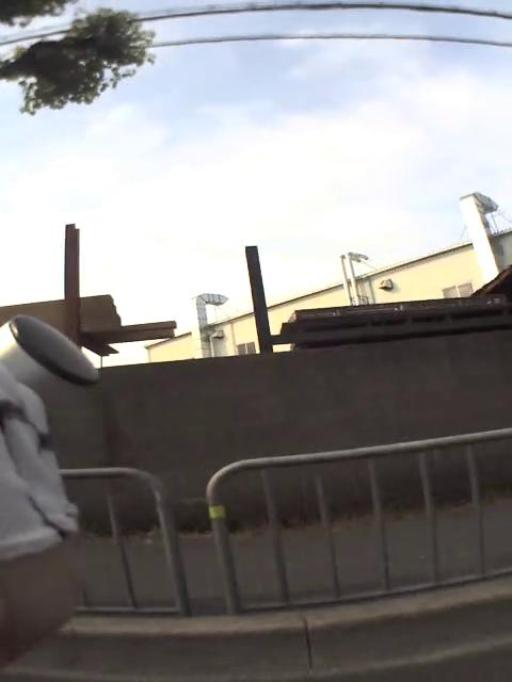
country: JP
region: Osaka
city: Kadoma
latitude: 34.7339
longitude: 135.5865
